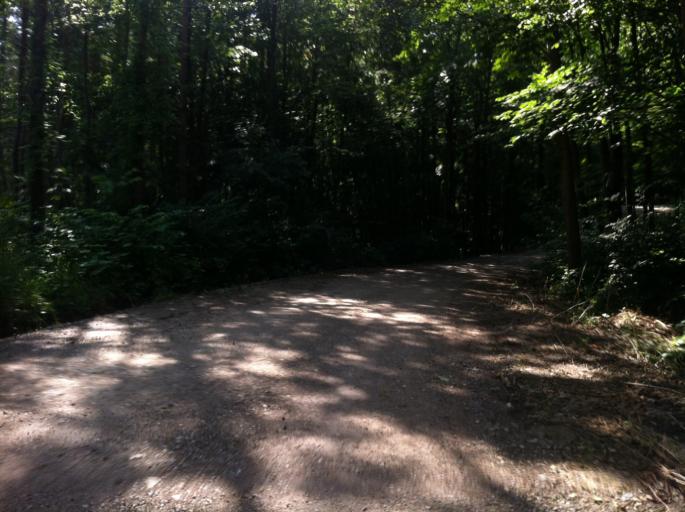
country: AT
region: Lower Austria
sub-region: Politischer Bezirk Modling
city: Laab im Walde
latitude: 48.1790
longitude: 16.1636
